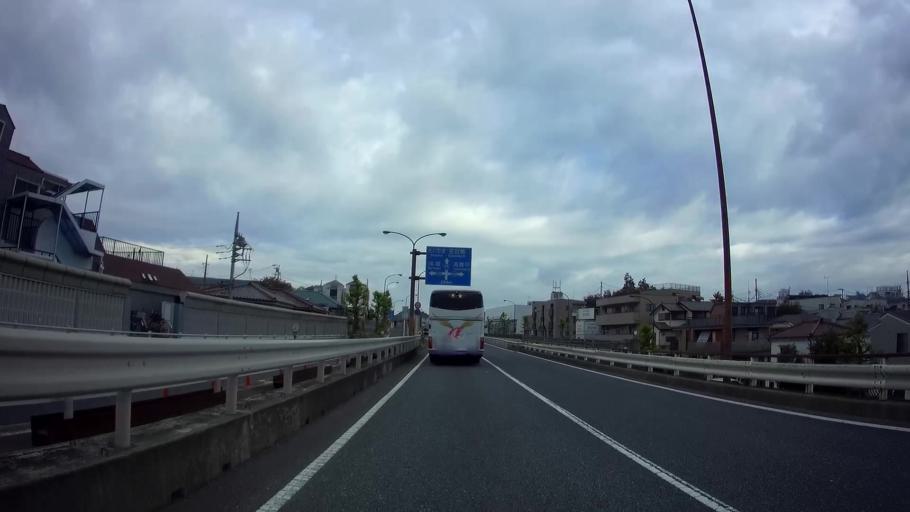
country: JP
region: Saitama
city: Wako
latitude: 35.7779
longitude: 139.6505
